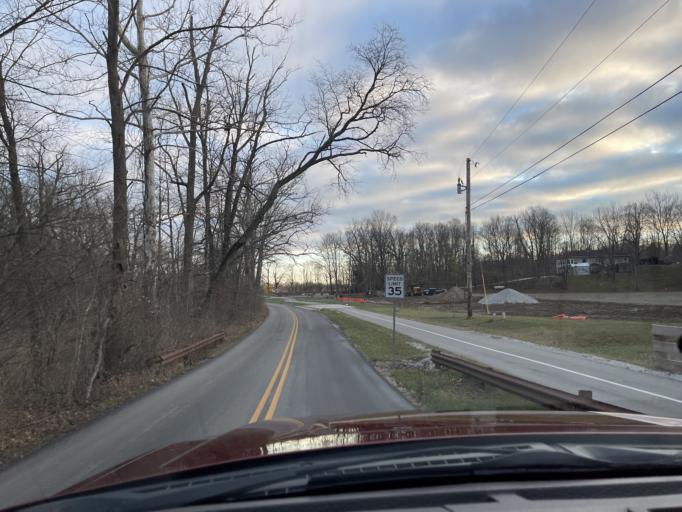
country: US
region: Indiana
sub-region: Hendricks County
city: Avon
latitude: 39.7750
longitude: -86.4212
